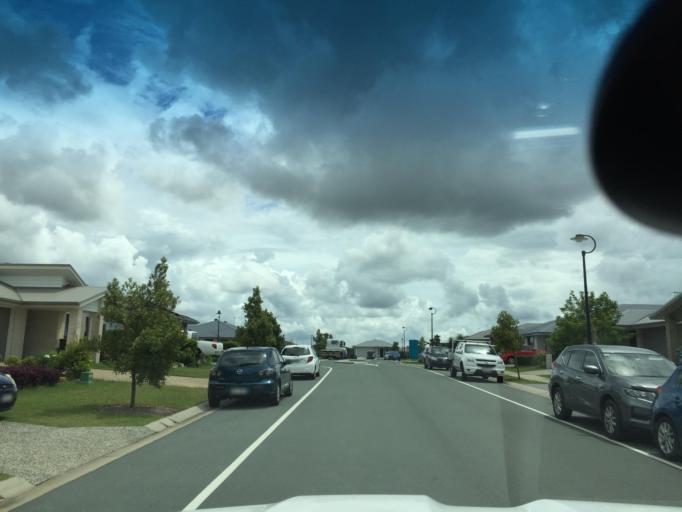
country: AU
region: Queensland
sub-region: Moreton Bay
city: Caboolture South
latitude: -27.0960
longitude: 152.9646
